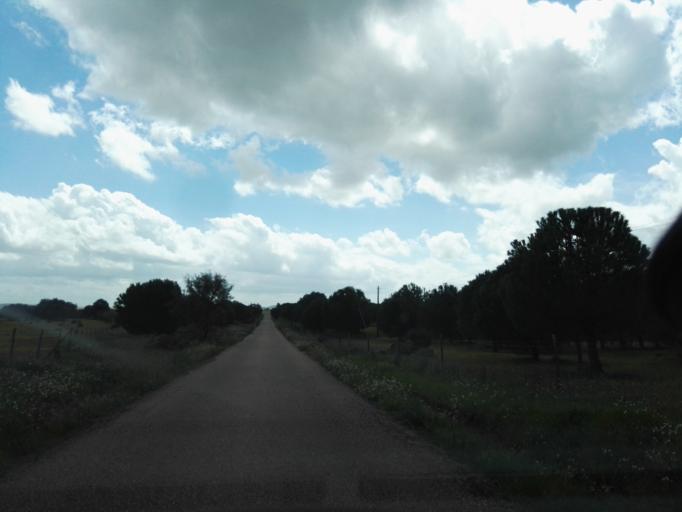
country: PT
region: Portalegre
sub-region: Elvas
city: Elvas
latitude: 38.9825
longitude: -7.1764
